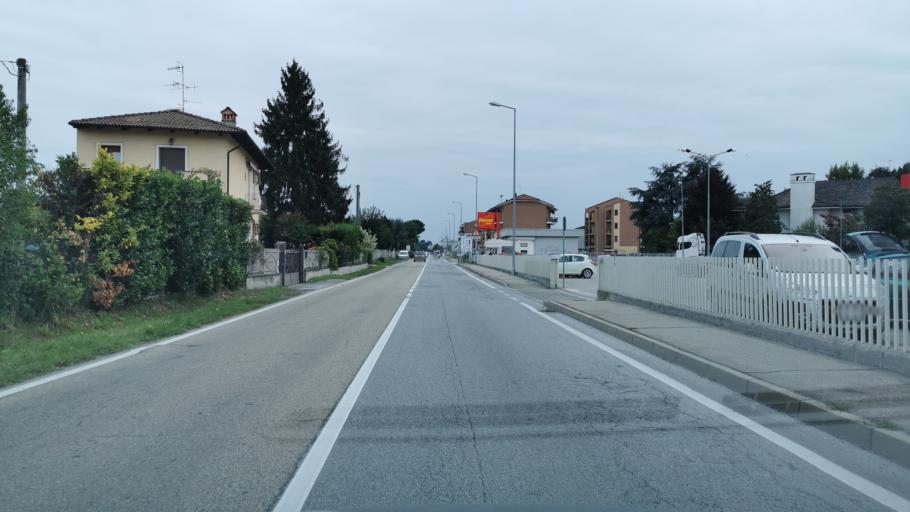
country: IT
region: Piedmont
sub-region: Provincia di Cuneo
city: Bra
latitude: 44.6825
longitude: 7.8484
